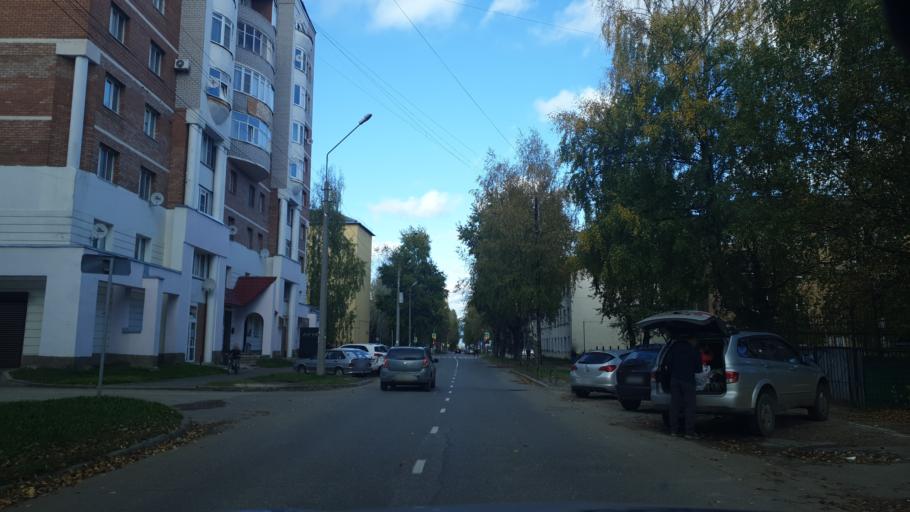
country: RU
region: Komi Republic
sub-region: Syktyvdinskiy Rayon
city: Syktyvkar
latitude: 61.6646
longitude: 50.8456
